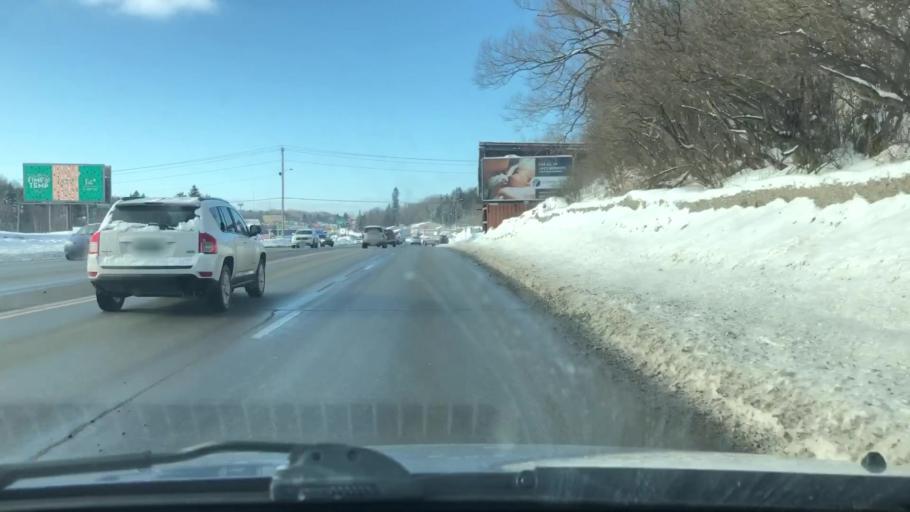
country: US
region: Minnesota
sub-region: Saint Louis County
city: Duluth
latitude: 46.8000
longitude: -92.1202
